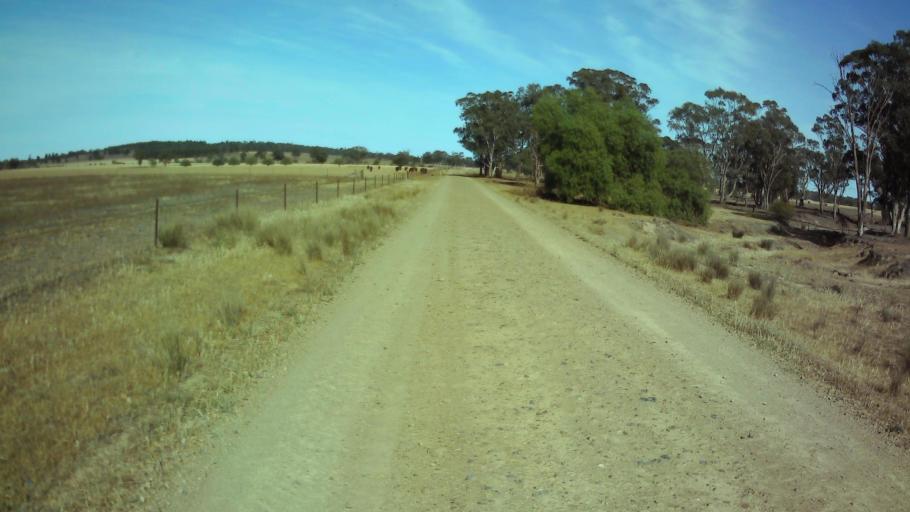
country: AU
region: New South Wales
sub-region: Weddin
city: Grenfell
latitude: -33.7824
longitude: 148.0683
